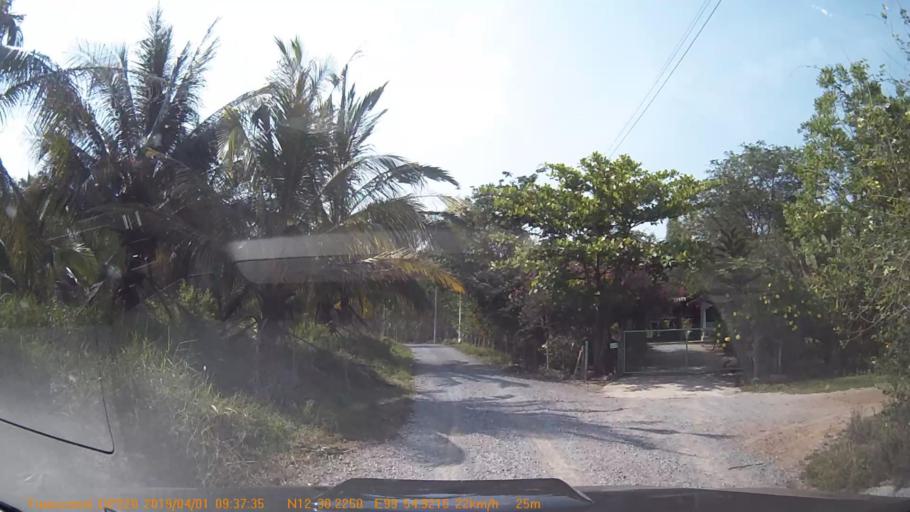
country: TH
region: Prachuap Khiri Khan
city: Hua Hin
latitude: 12.5036
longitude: 99.9154
